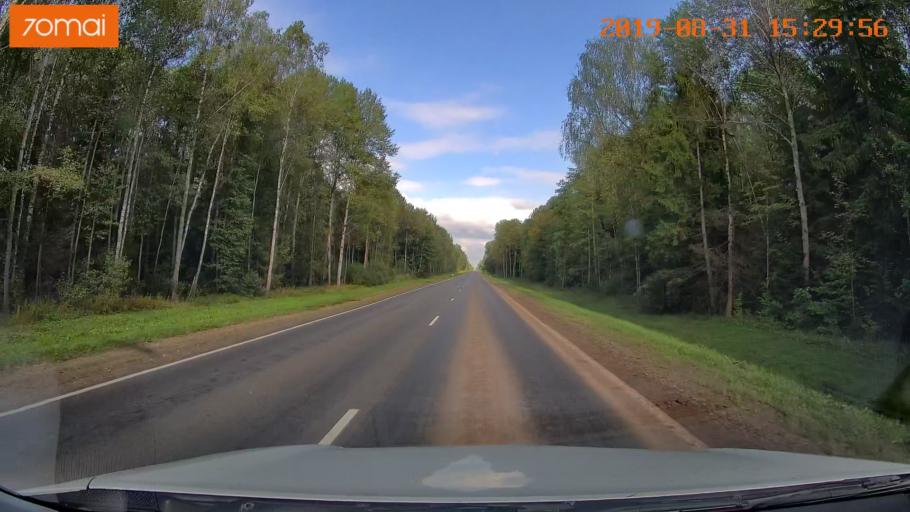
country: RU
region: Kaluga
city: Baryatino
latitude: 54.5723
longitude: 34.6178
